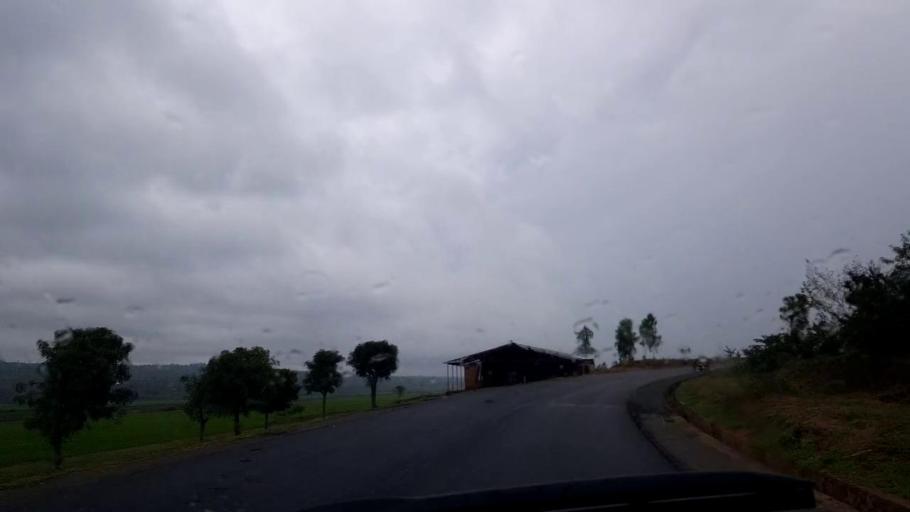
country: RW
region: Northern Province
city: Byumba
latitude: -1.4063
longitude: 30.2846
